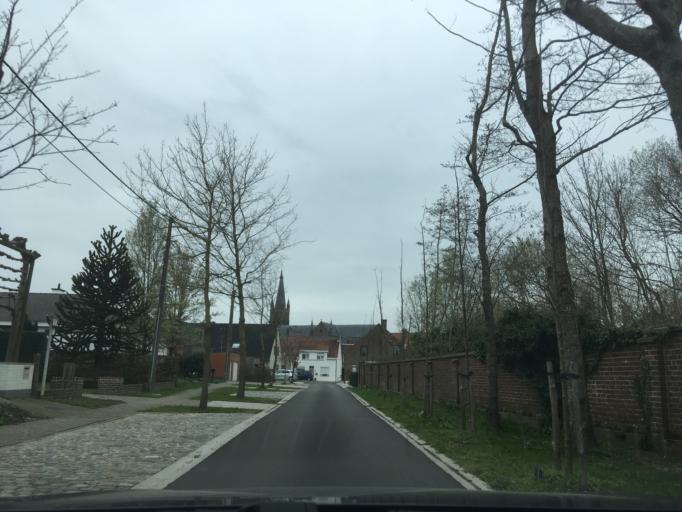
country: BE
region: Flanders
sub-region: Provincie West-Vlaanderen
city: Lichtervelde
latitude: 51.0252
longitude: 3.1438
